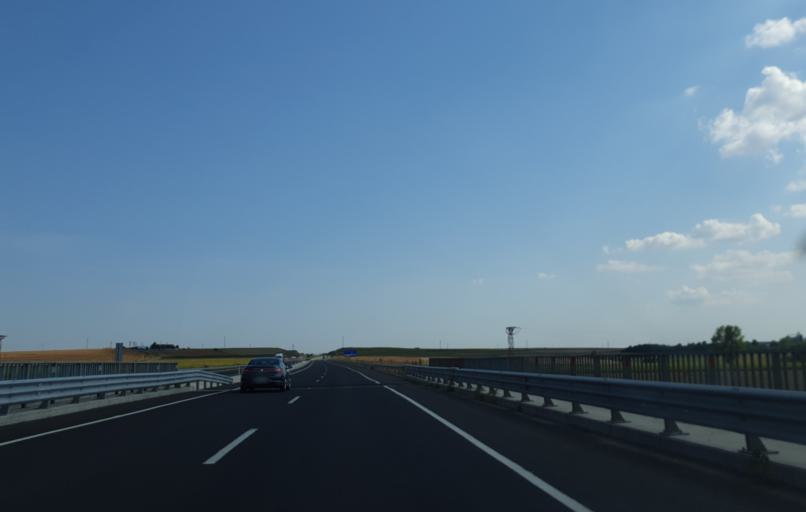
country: TR
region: Tekirdag
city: Muratli
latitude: 41.2177
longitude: 27.5326
